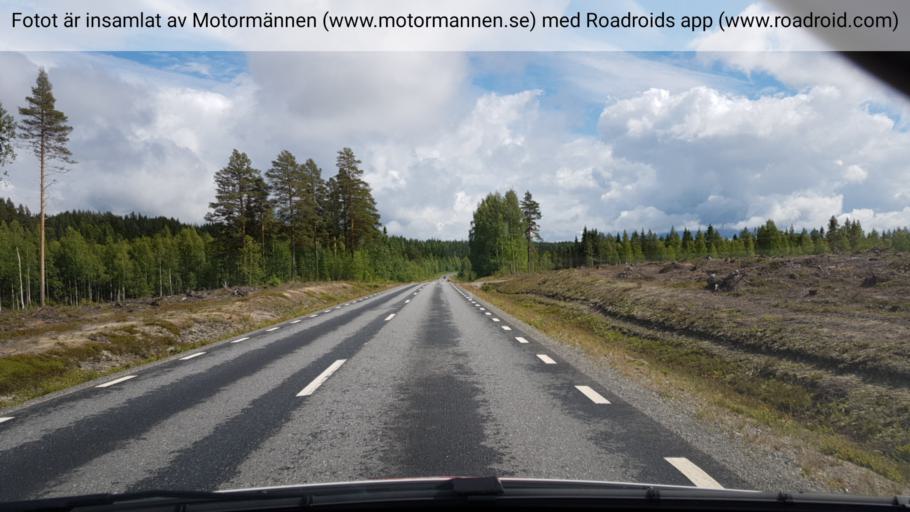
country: SE
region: Vaesterbotten
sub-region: Bjurholms Kommun
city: Bjurholm
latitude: 64.3826
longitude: 19.1218
